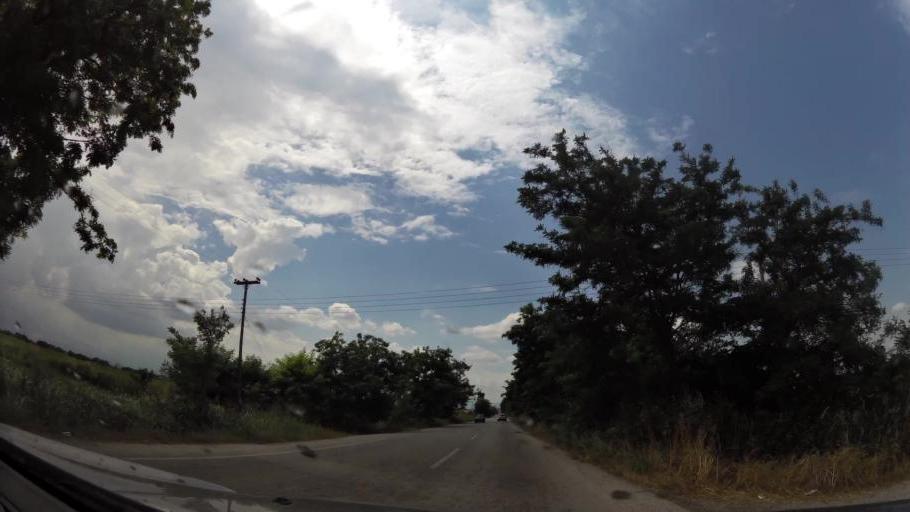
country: GR
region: Central Macedonia
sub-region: Nomos Pierias
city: Korinos
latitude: 40.3111
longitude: 22.6030
